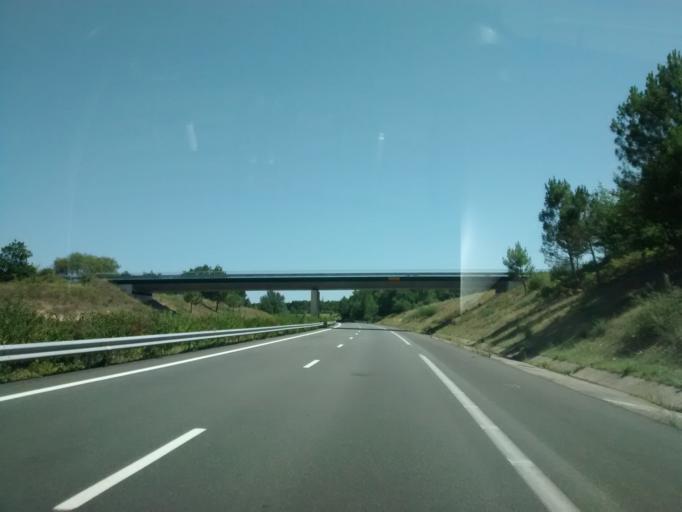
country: FR
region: Aquitaine
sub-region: Departement de la Dordogne
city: Le Pizou
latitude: 44.9890
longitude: 0.0518
